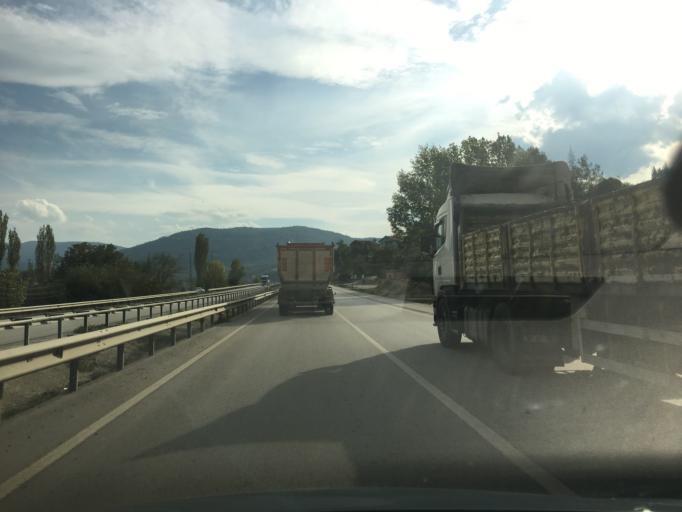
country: TR
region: Karabuk
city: Karabuk
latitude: 41.1145
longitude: 32.6711
